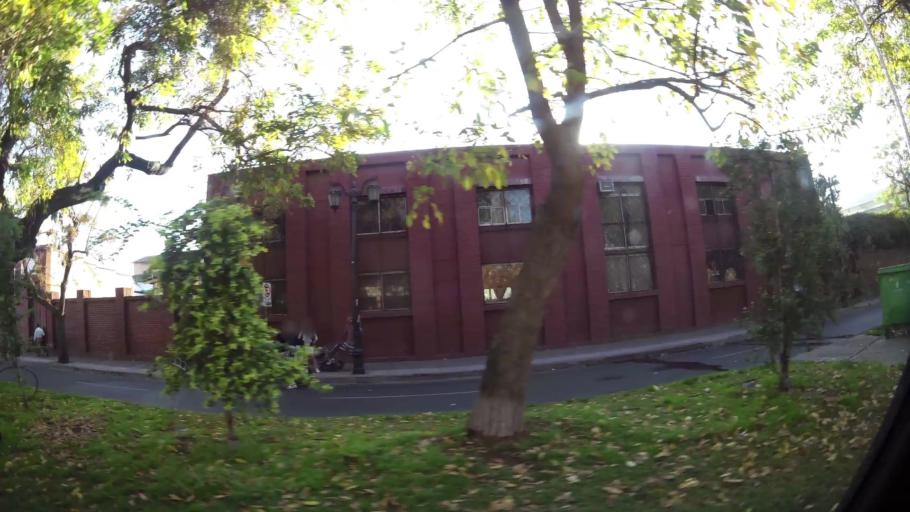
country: CL
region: Santiago Metropolitan
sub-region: Provincia de Santiago
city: Santiago
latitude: -33.4314
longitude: -70.6693
